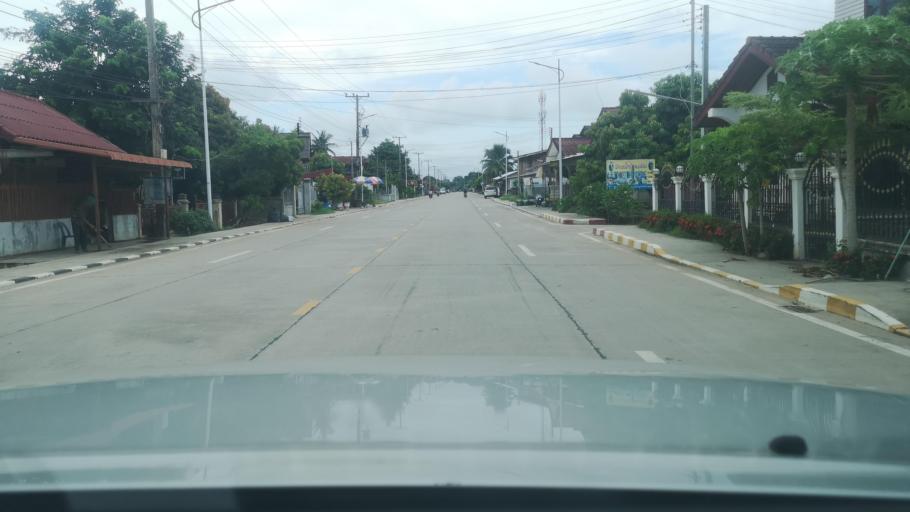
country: TH
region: Nong Khai
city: Tha Bo
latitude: 17.8295
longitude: 102.6491
